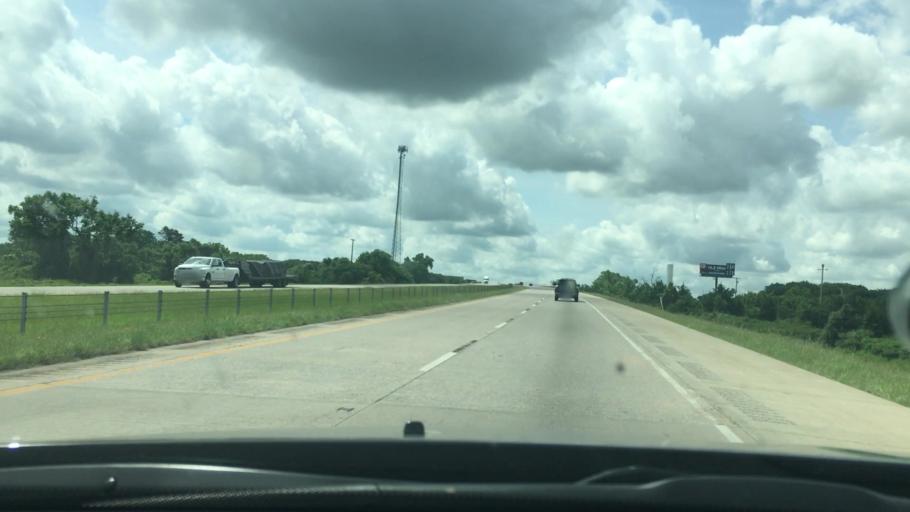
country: US
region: Oklahoma
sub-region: Love County
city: Marietta
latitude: 33.8409
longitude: -97.1335
